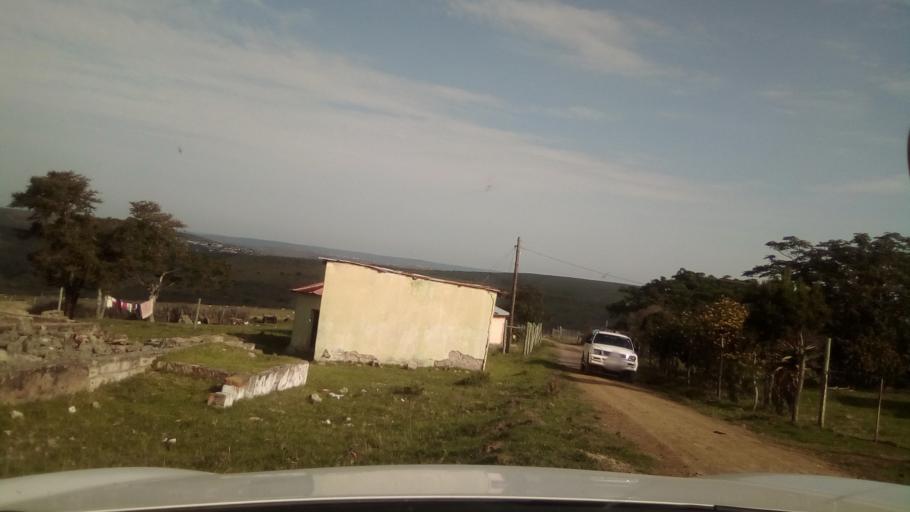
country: ZA
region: Eastern Cape
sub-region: Buffalo City Metropolitan Municipality
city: Bhisho
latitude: -33.0070
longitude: 27.3015
